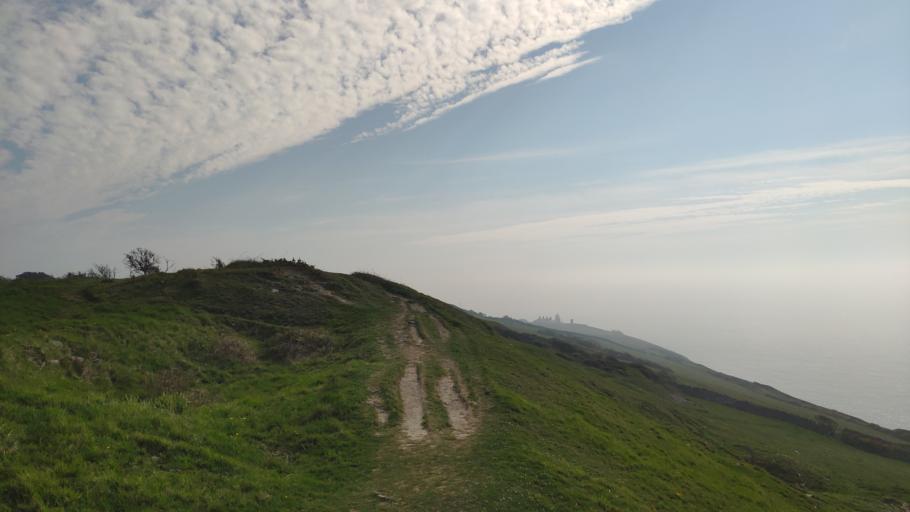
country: GB
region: England
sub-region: Dorset
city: Swanage
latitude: 50.5927
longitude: -1.9704
